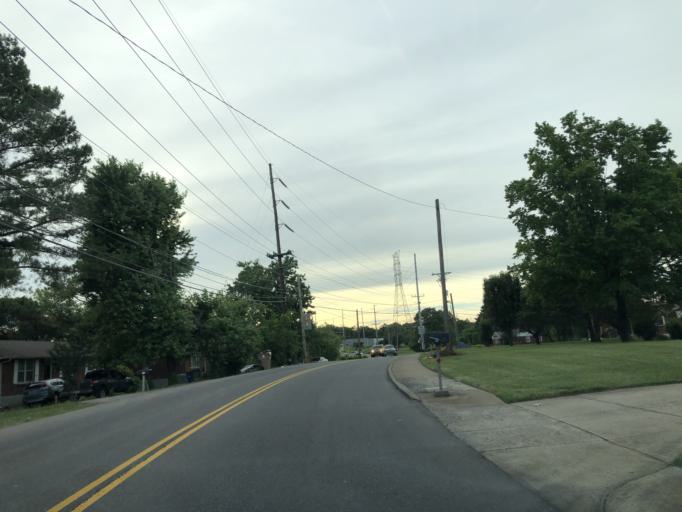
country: US
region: Tennessee
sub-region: Davidson County
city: Goodlettsville
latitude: 36.2957
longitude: -86.7101
